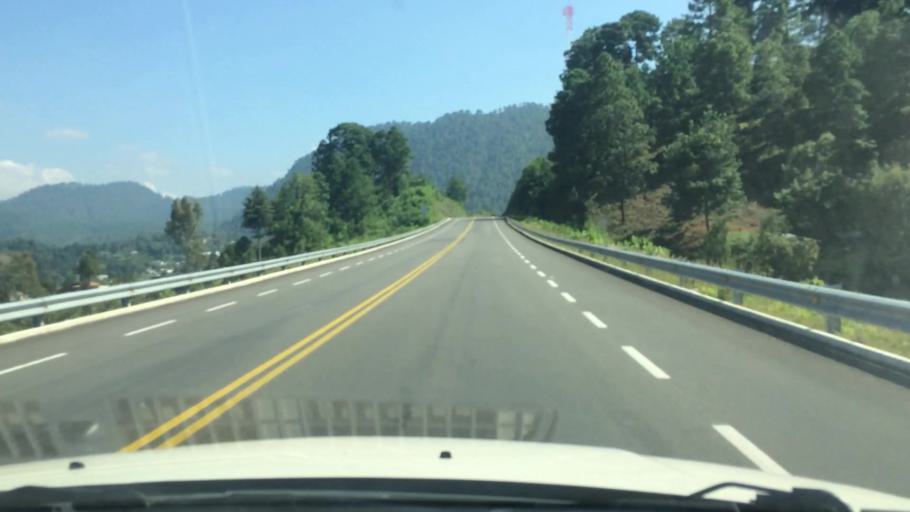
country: MX
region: Mexico
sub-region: Amanalco
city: Polvillos (San Bartolo Quinta Seccion)
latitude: 19.2251
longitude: -100.0845
